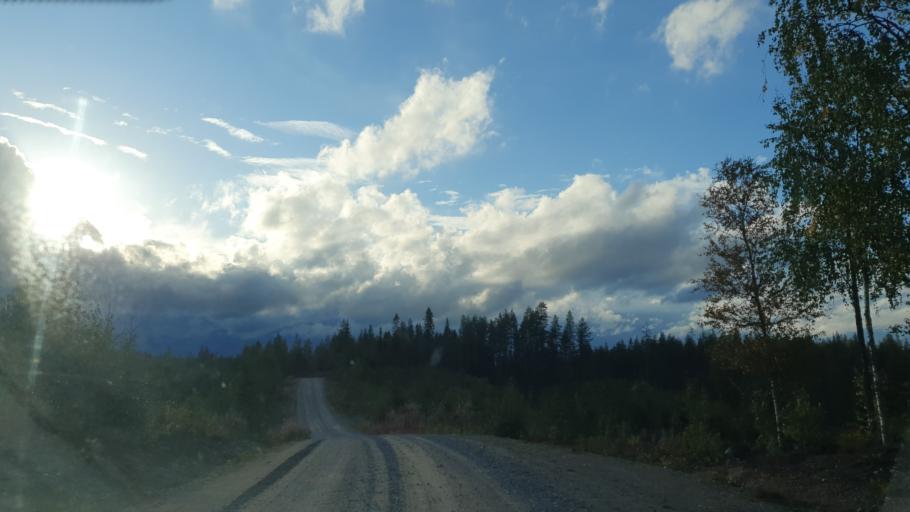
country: FI
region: Kainuu
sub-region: Kehys-Kainuu
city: Kuhmo
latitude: 64.3364
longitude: 29.9581
